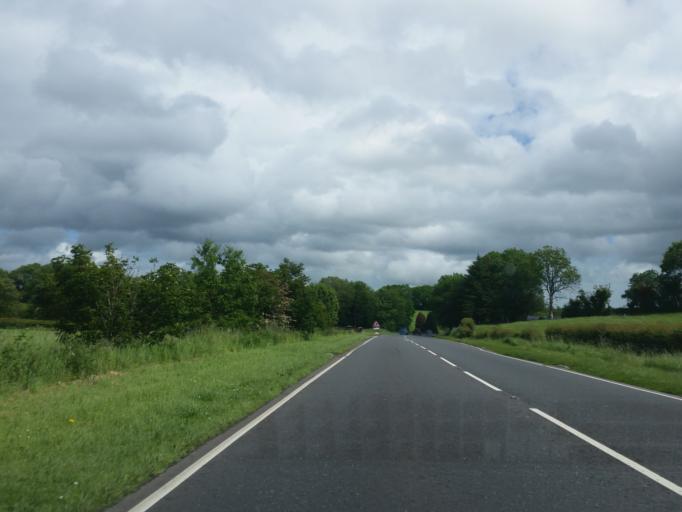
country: IE
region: Ulster
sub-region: County Monaghan
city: Monaghan
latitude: 54.4732
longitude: -7.0577
